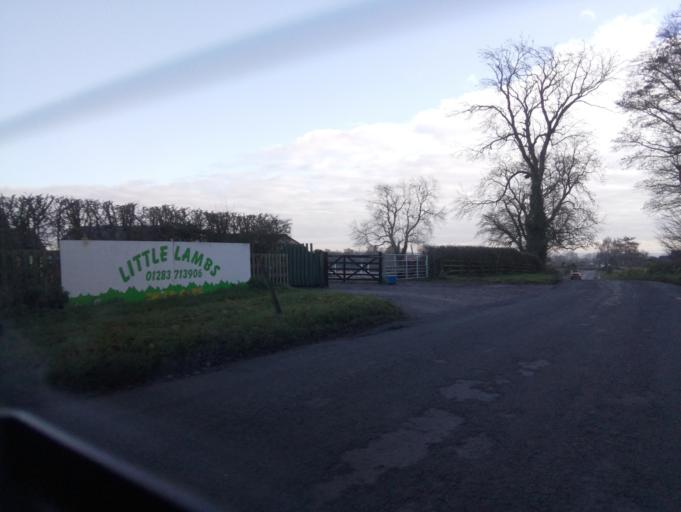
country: GB
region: England
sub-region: Staffordshire
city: Barton under Needwood
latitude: 52.8006
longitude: -1.7181
